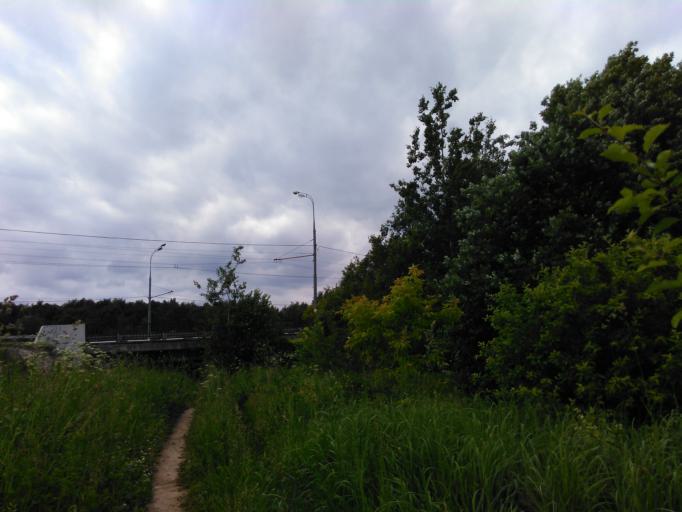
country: RU
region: Moscow
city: Yasenevo
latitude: 55.6281
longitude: 37.5415
